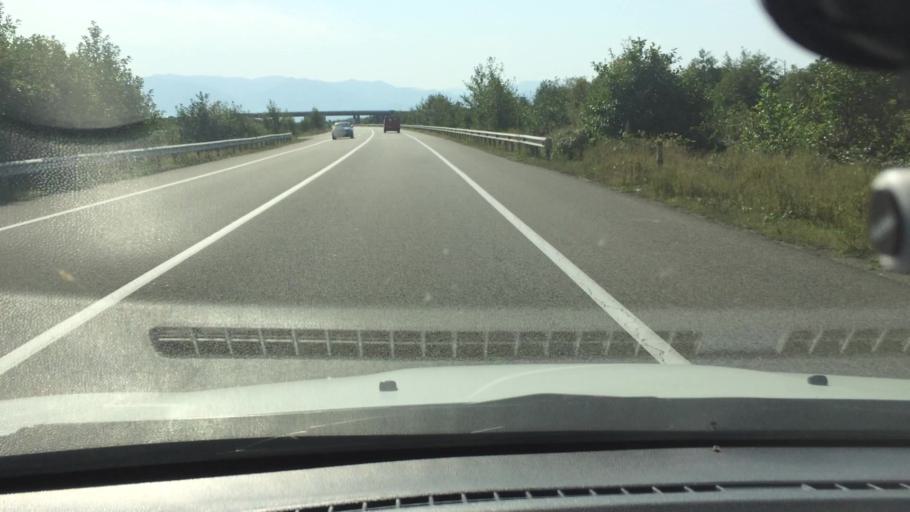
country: GE
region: Guria
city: Urek'i
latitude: 41.9217
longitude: 41.7743
